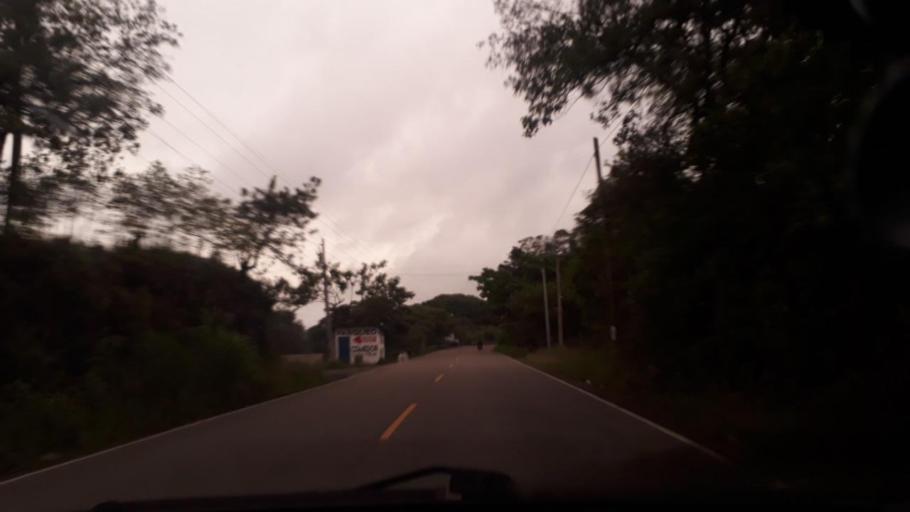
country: GT
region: Chiquimula
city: Esquipulas
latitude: 14.5445
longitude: -89.2851
